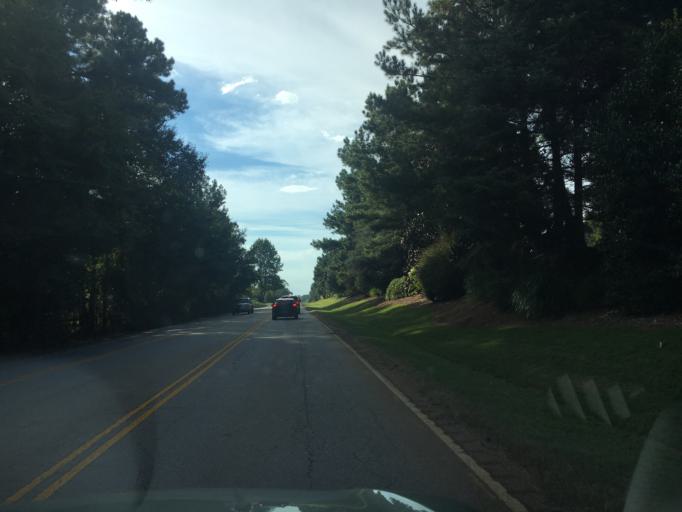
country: US
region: South Carolina
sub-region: Greenville County
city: Five Forks
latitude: 34.8035
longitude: -82.2107
